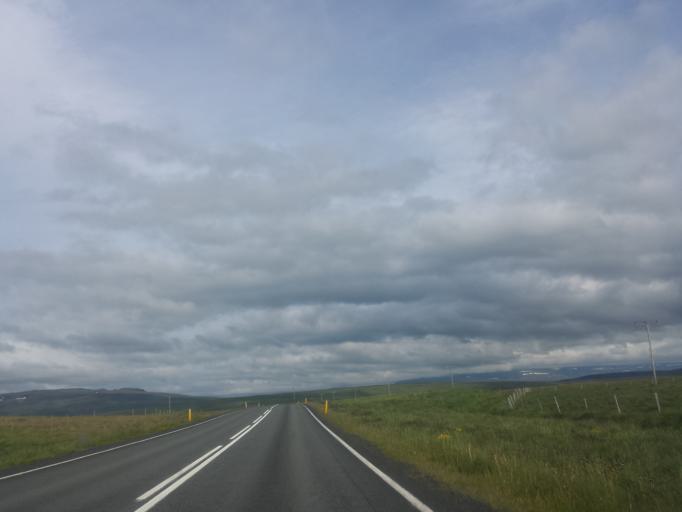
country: IS
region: West
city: Borgarnes
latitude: 65.3120
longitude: -20.9479
